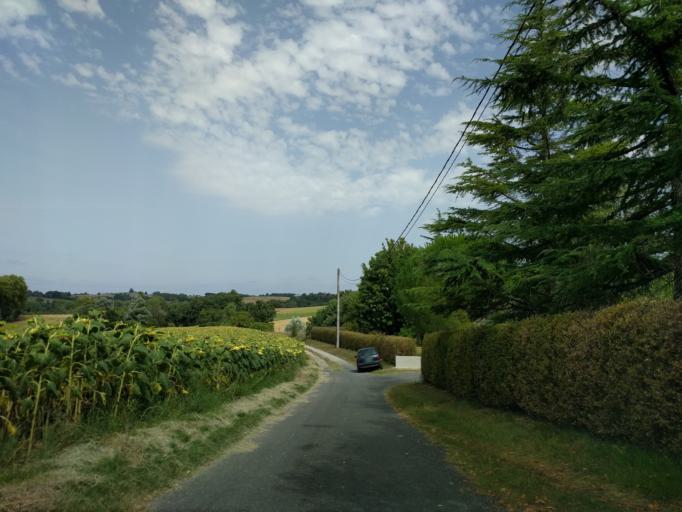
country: FR
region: Midi-Pyrenees
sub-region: Departement du Tarn
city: Saix
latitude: 43.6366
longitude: 2.1996
